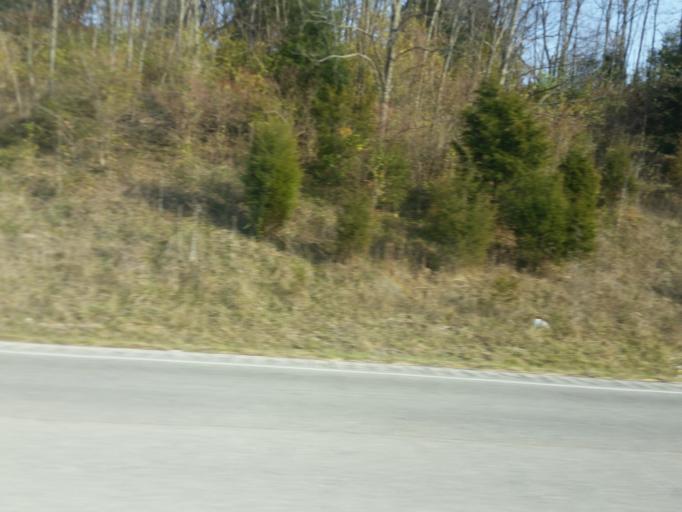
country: US
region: Kentucky
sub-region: Harrison County
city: Cynthiana
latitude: 38.4651
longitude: -84.2855
